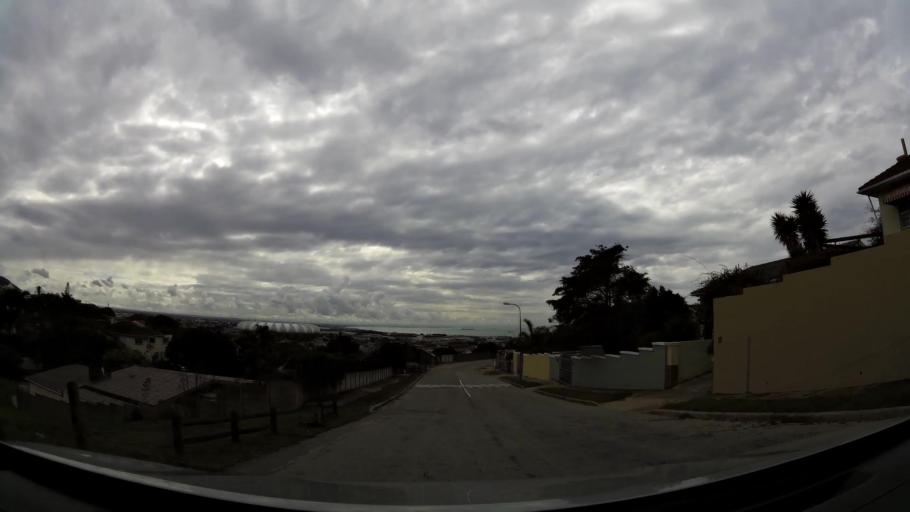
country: ZA
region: Eastern Cape
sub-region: Nelson Mandela Bay Metropolitan Municipality
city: Port Elizabeth
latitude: -33.9476
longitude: 25.5969
